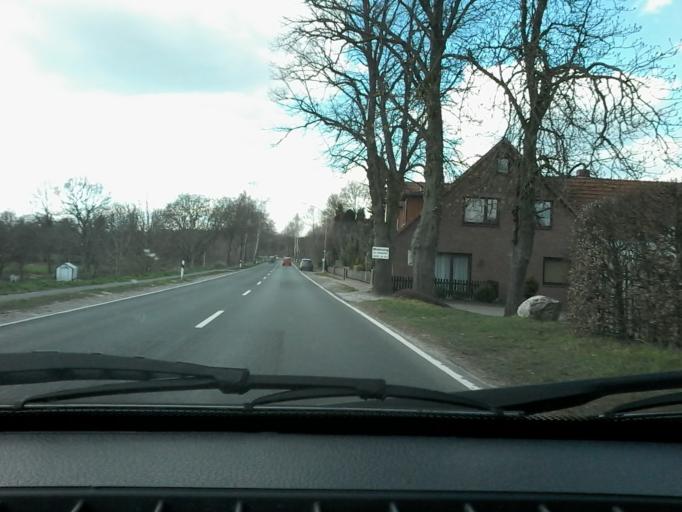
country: DE
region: Lower Saxony
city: Langwedel
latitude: 52.9932
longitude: 9.1301
